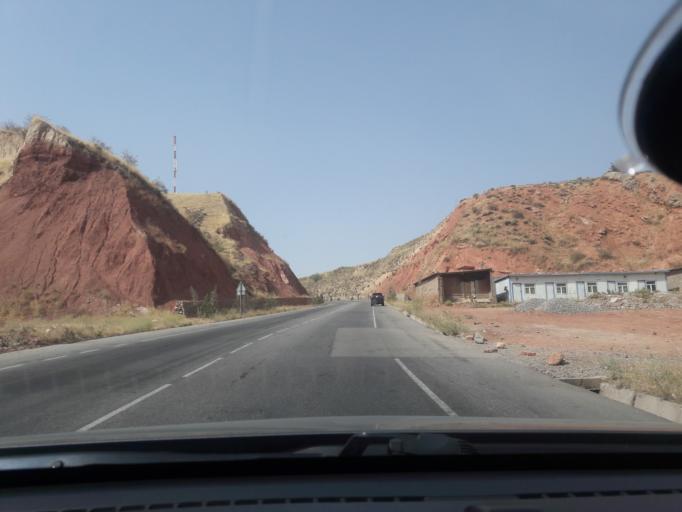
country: TJ
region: Republican Subordination
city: Vahdat
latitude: 38.4886
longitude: 69.1750
